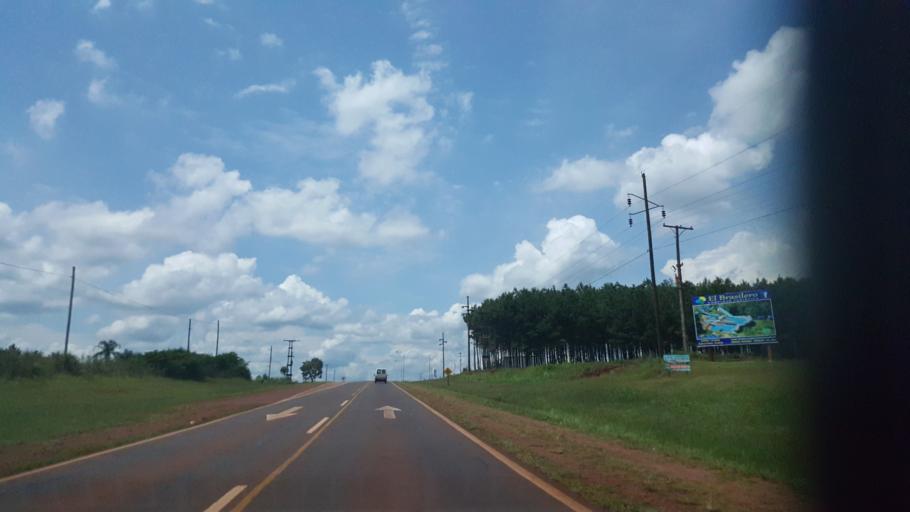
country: AR
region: Misiones
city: Puerto Rico
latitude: -26.8207
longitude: -55.0032
